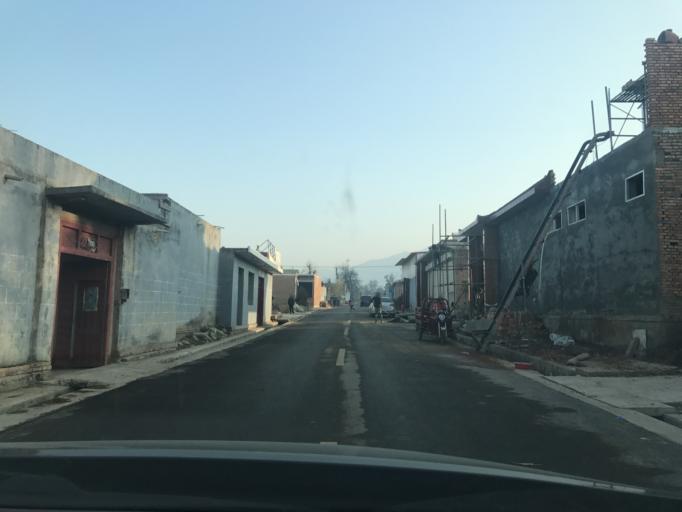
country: CN
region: Gansu Sheng
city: Maji
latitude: 35.4003
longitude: 103.0566
